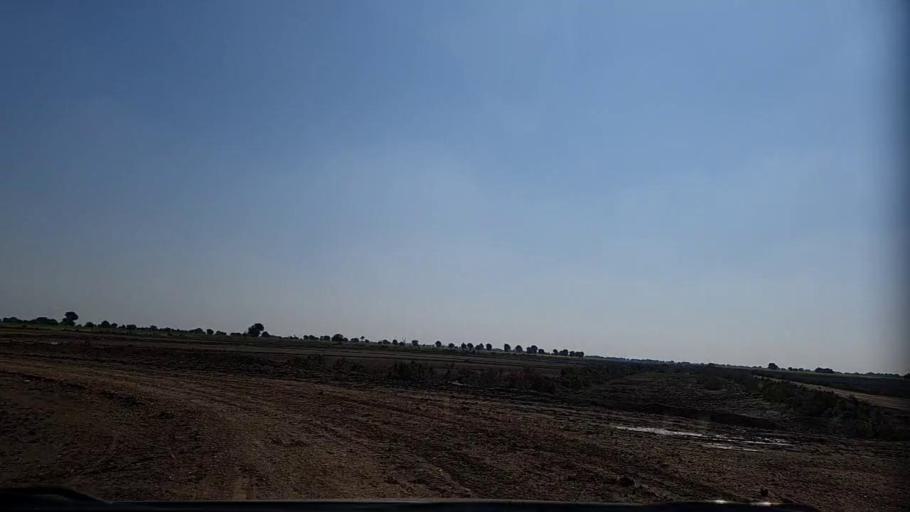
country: PK
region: Sindh
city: Pithoro
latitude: 25.6843
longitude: 69.3559
